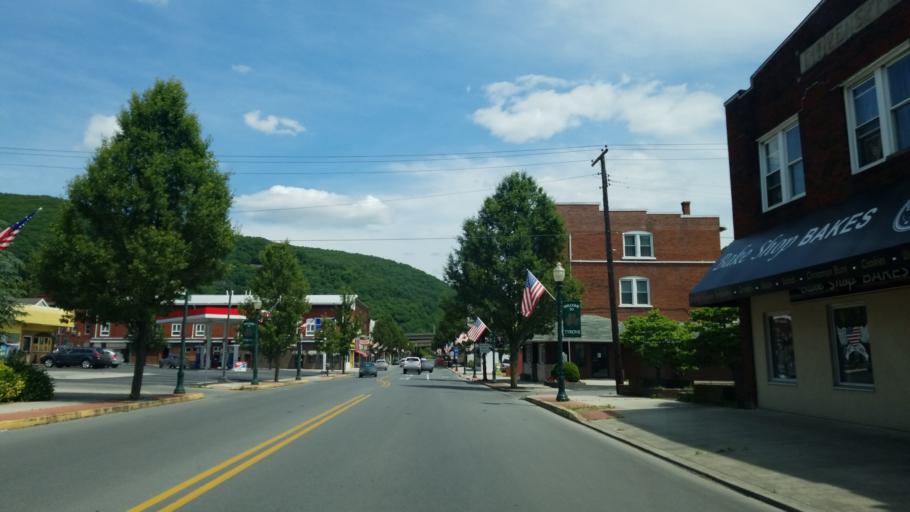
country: US
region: Pennsylvania
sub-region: Blair County
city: Tyrone
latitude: 40.6711
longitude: -78.2410
